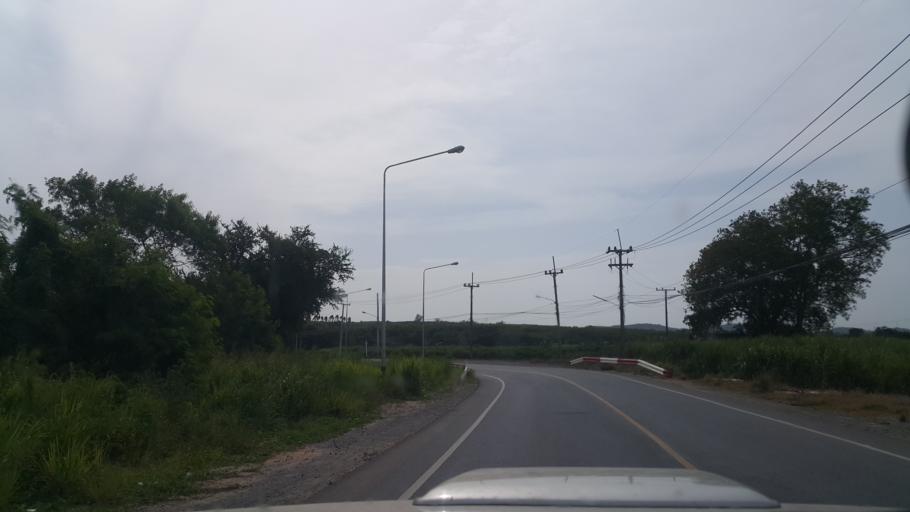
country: TH
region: Rayong
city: Ban Chang
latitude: 12.7668
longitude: 101.0147
